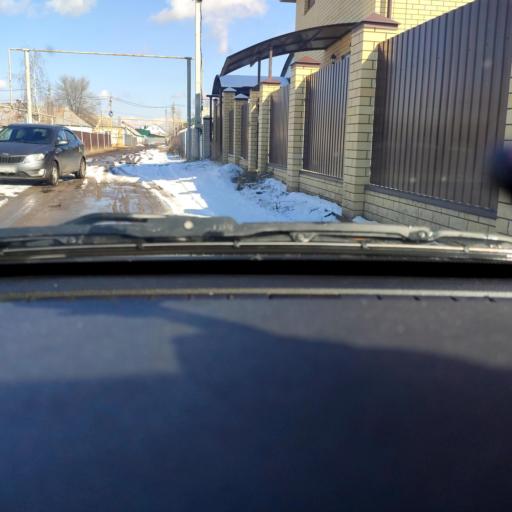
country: RU
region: Voronezj
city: Somovo
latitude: 51.7507
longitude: 39.3312
